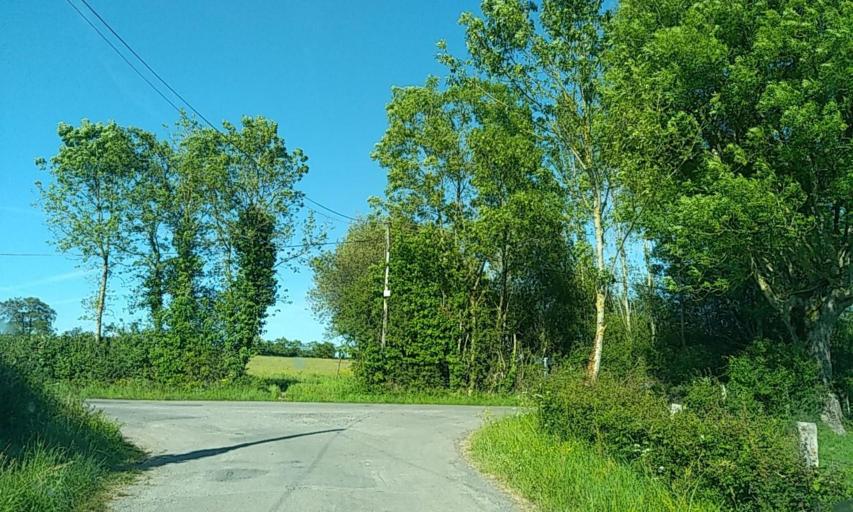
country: FR
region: Poitou-Charentes
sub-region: Departement des Deux-Sevres
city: Boisme
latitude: 46.7856
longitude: -0.4196
